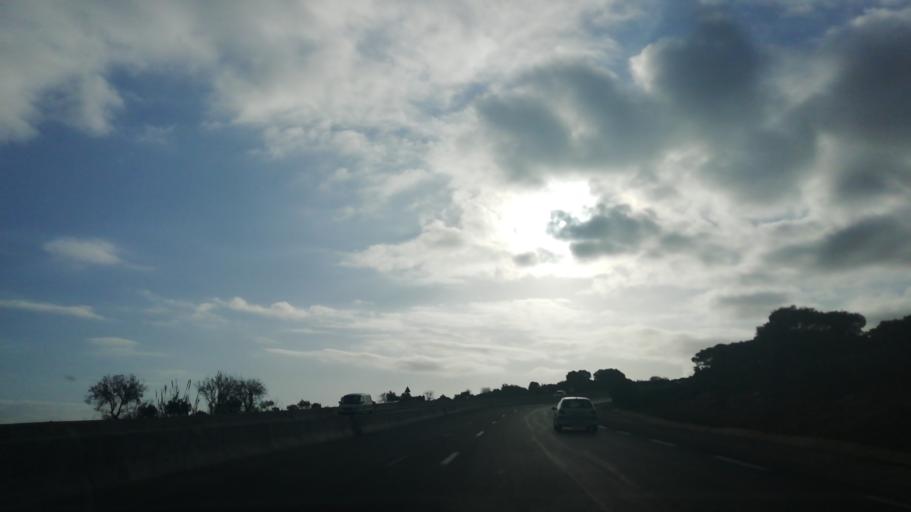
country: DZ
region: Mostaganem
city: Mostaganem
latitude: 36.1099
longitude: 0.2621
